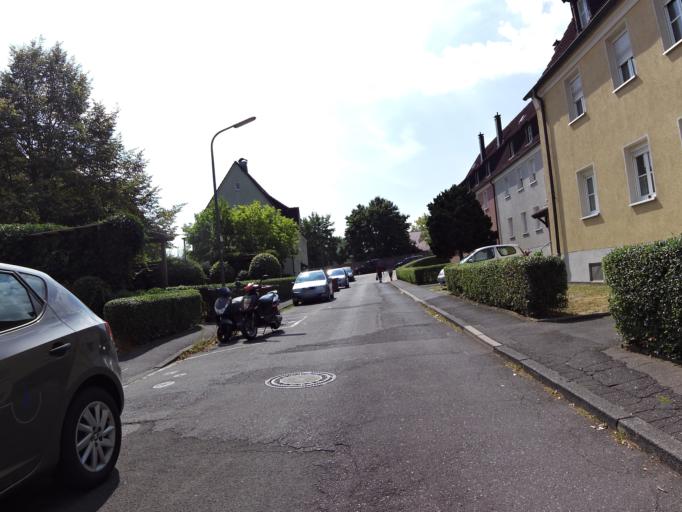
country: DE
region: Bavaria
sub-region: Regierungsbezirk Unterfranken
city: Zell am Main
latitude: 49.8150
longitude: 9.8697
